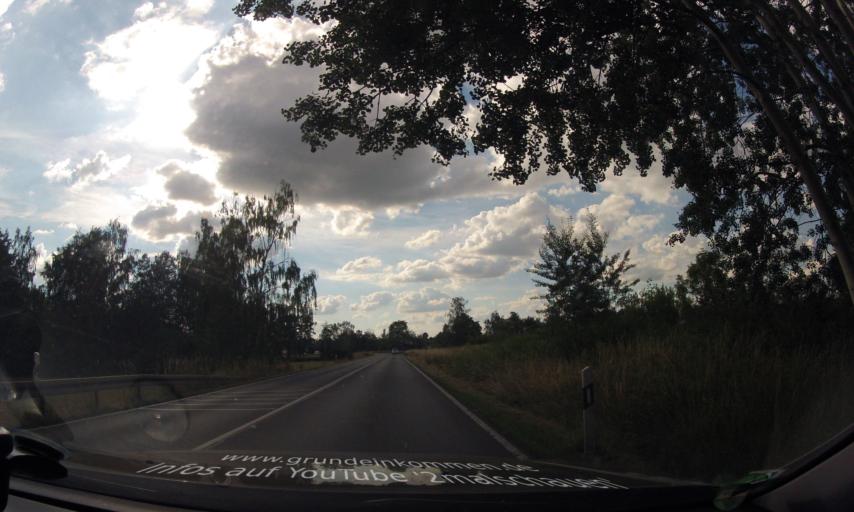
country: DE
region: Saxony
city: Bennewitz
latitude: 51.3604
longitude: 12.6888
